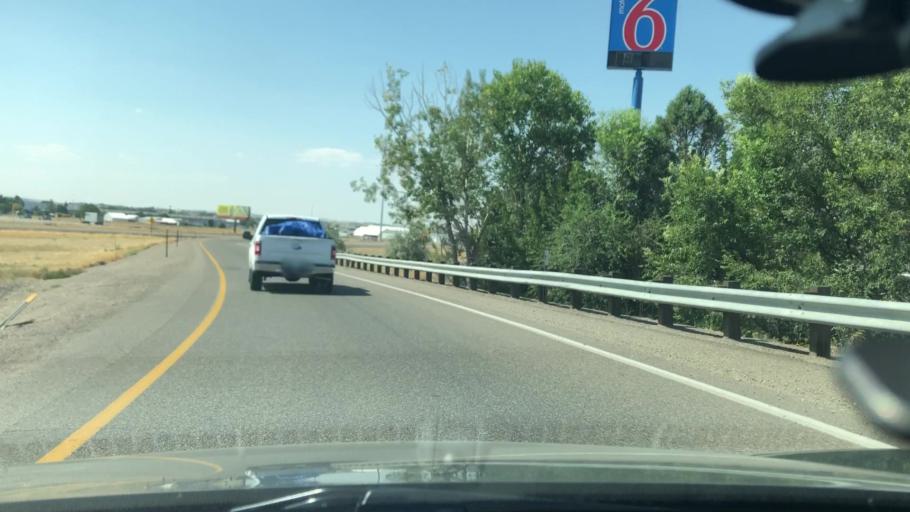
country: US
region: Oregon
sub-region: Malheur County
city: Ontario
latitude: 44.0262
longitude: -116.9475
